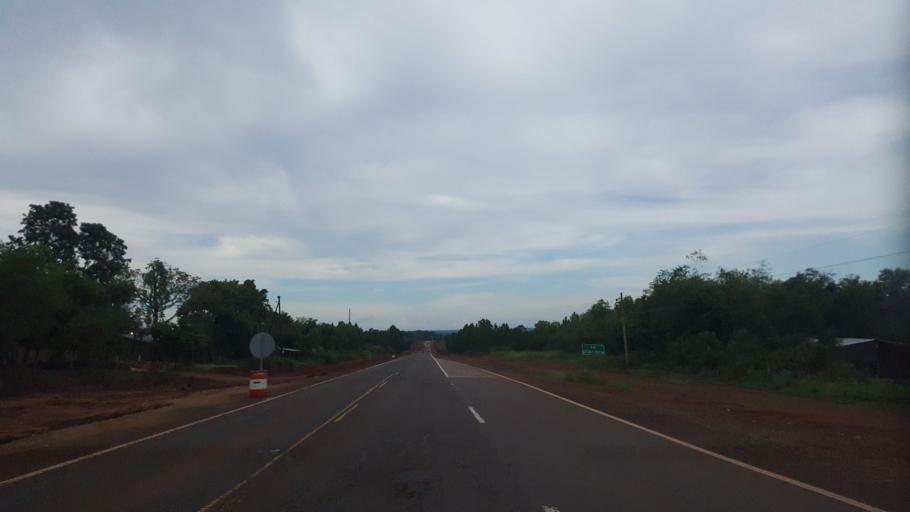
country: AR
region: Misiones
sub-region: Departamento de Candelaria
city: Loreto
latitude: -27.3487
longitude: -55.5476
